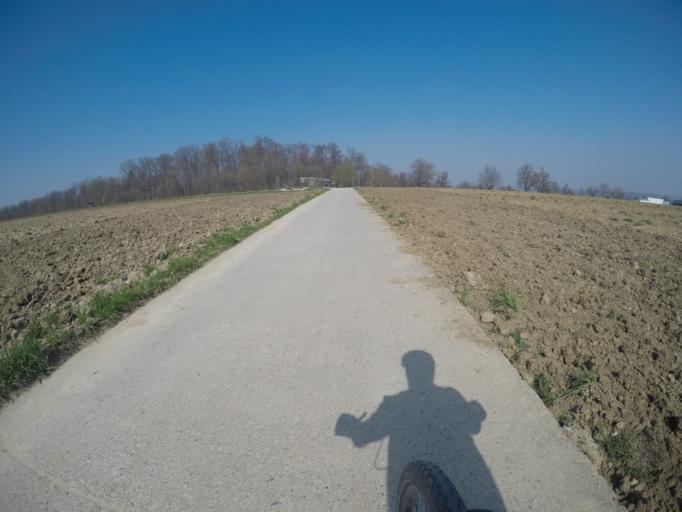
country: DE
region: Baden-Wuerttemberg
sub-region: Regierungsbezirk Stuttgart
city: Altdorf
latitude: 48.5913
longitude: 9.2648
